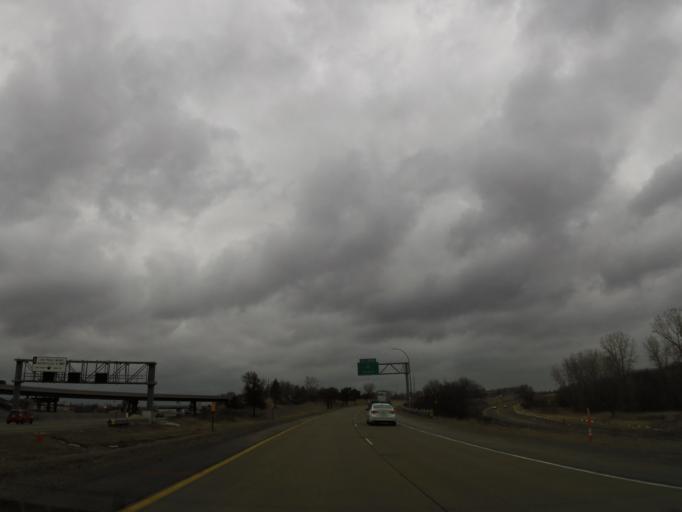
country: US
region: Minnesota
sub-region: Dakota County
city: Burnsville
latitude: 44.7381
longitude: -93.2829
